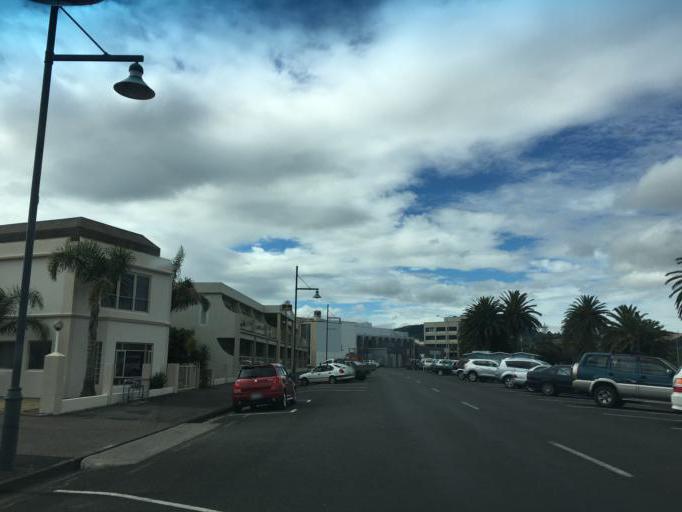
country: NZ
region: Gisborne
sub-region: Gisborne District
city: Gisborne
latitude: -38.6704
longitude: 178.0275
